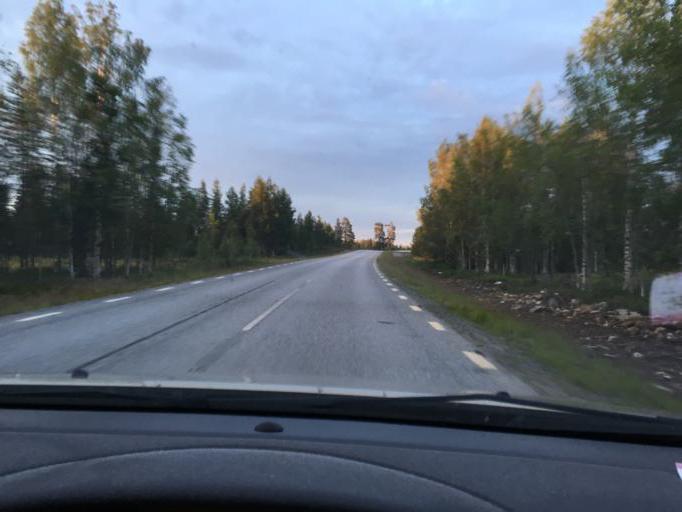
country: SE
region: Norrbotten
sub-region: Kalix Kommun
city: Toere
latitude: 66.0559
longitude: 22.4488
